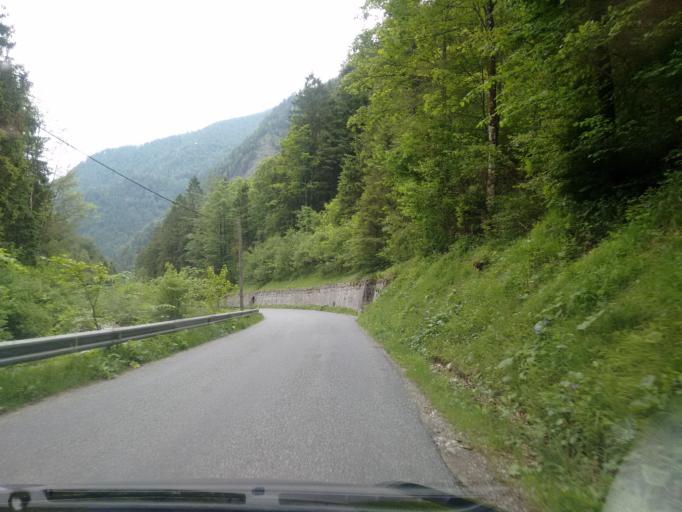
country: AT
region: Upper Austria
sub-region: Politischer Bezirk Gmunden
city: Ebensee
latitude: 47.8232
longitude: 13.7432
